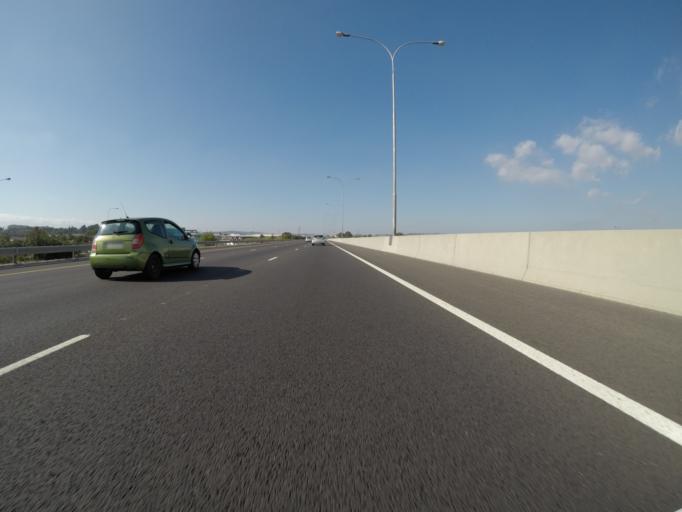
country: ZA
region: Western Cape
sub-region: City of Cape Town
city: Kraaifontein
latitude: -33.9163
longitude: 18.6673
